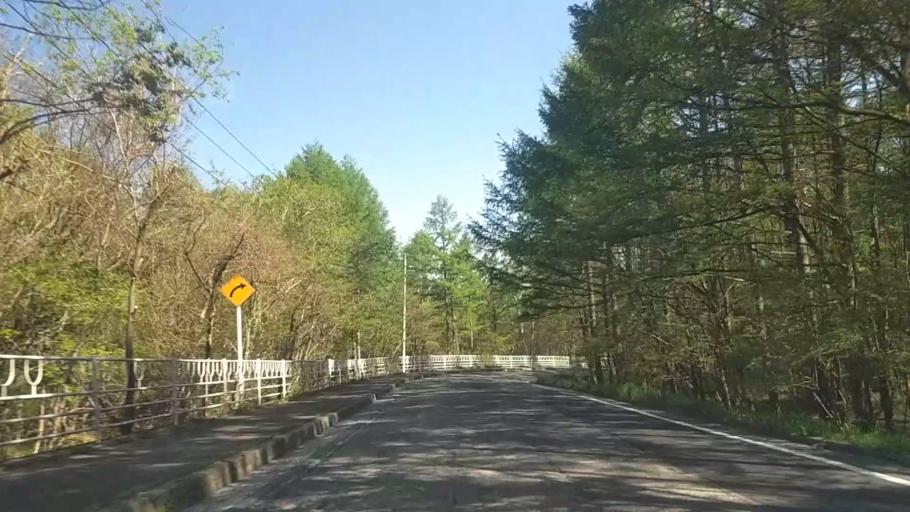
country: JP
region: Yamanashi
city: Nirasaki
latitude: 35.9303
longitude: 138.4190
